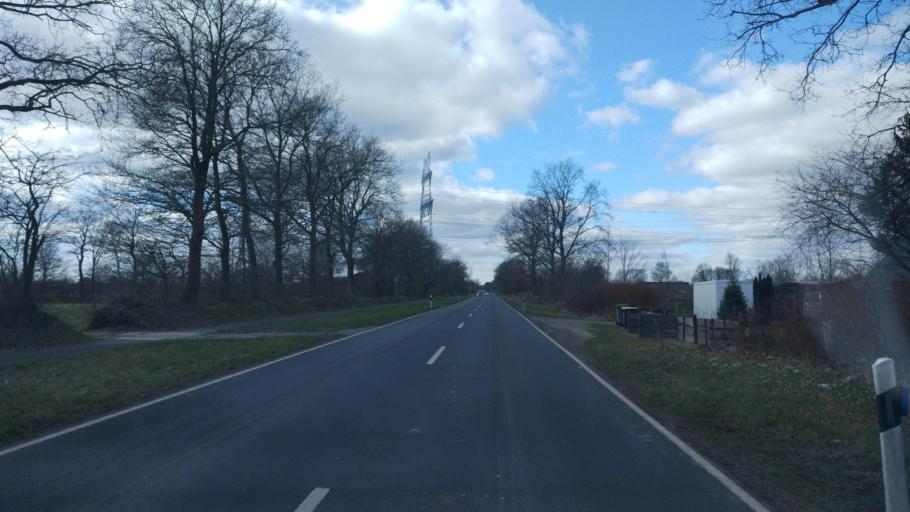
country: DE
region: Schleswig-Holstein
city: Gross Rheide
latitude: 54.4447
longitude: 9.4268
